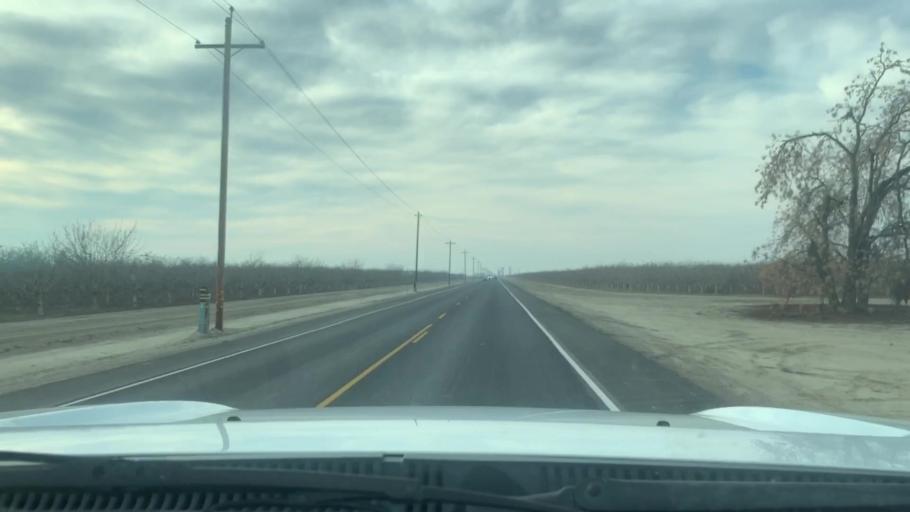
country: US
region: California
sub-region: Kern County
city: Buttonwillow
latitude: 35.4423
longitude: -119.4223
